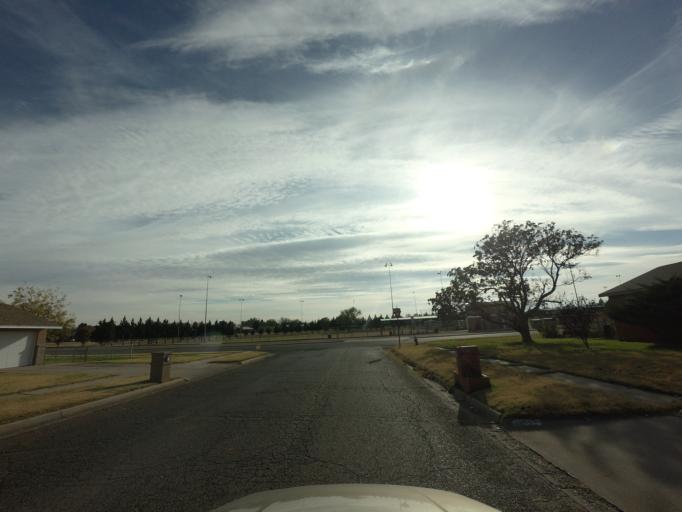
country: US
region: New Mexico
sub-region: Curry County
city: Clovis
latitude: 34.4258
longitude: -103.2266
